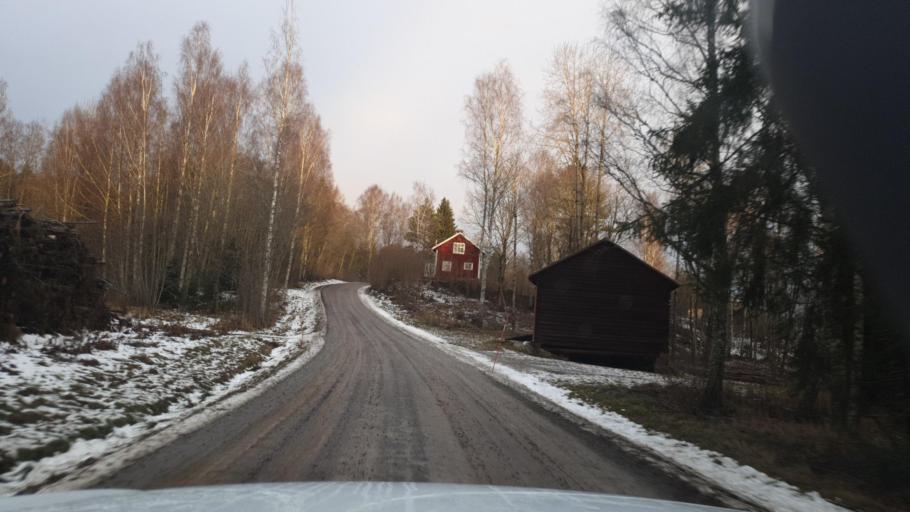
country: SE
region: Vaermland
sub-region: Eda Kommun
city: Amotfors
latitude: 59.7637
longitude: 12.2598
